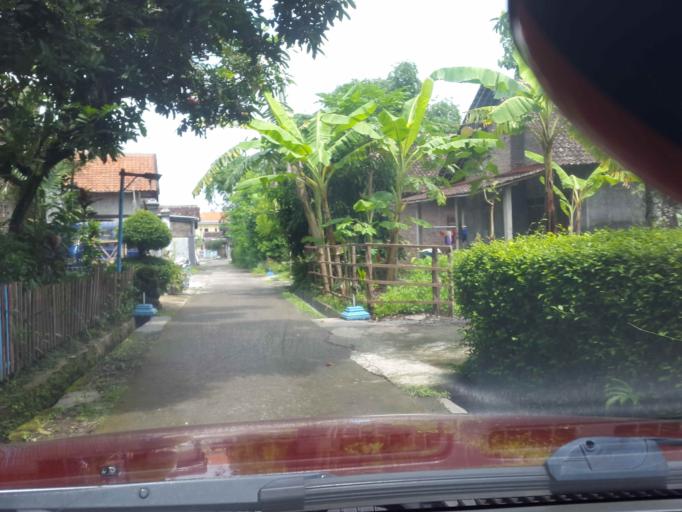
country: ID
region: Central Java
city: Jaten
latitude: -7.5988
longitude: 110.9433
